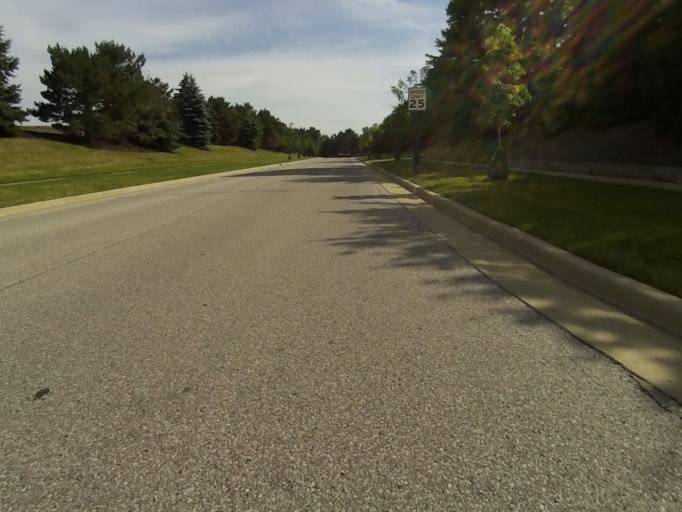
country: US
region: Ohio
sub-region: Summit County
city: Hudson
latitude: 41.2008
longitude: -81.4336
